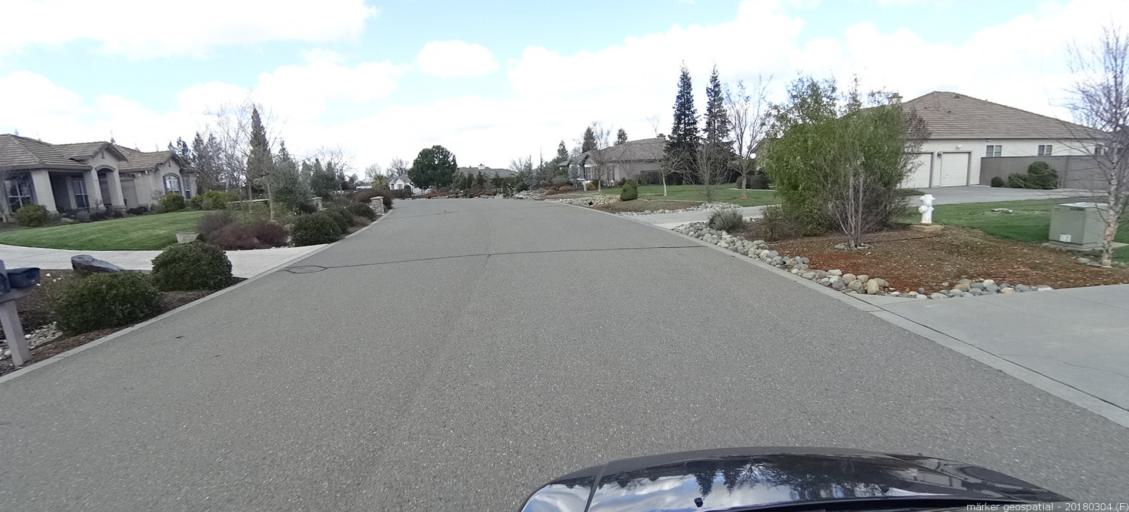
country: US
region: California
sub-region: Sacramento County
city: Vineyard
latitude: 38.4623
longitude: -121.2992
